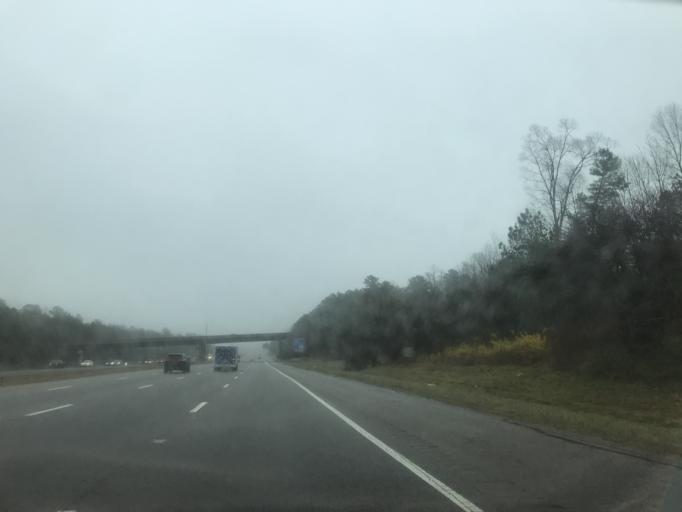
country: US
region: North Carolina
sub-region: Wake County
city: Morrisville
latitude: 35.8974
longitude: -78.7863
